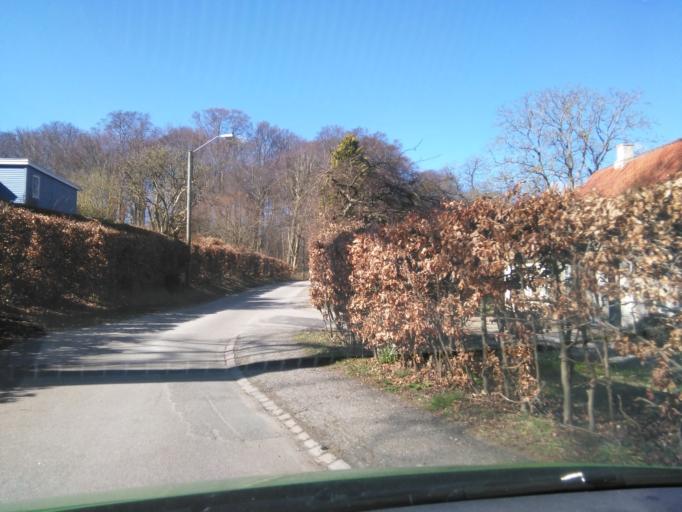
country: DK
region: Central Jutland
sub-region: Arhus Kommune
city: Arhus
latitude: 56.1243
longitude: 10.2010
